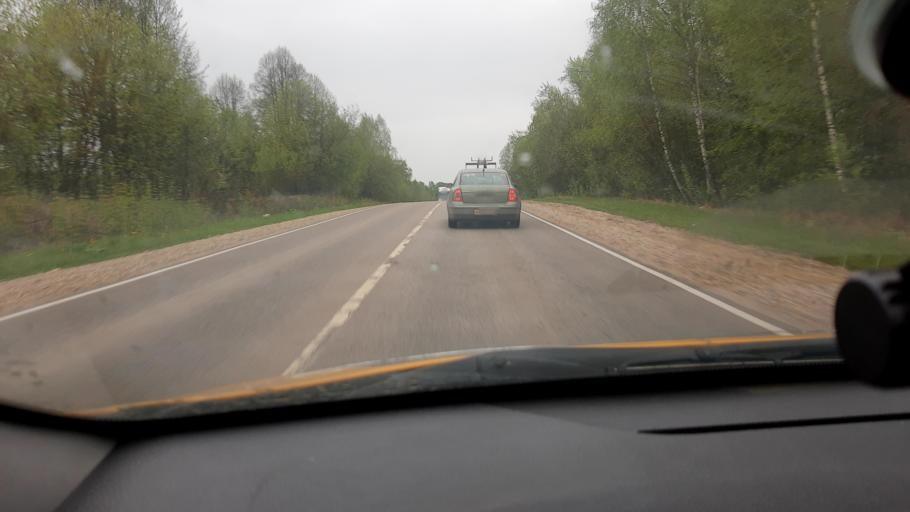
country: RU
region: Tula
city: Zaokskiy
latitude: 54.7768
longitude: 37.4351
